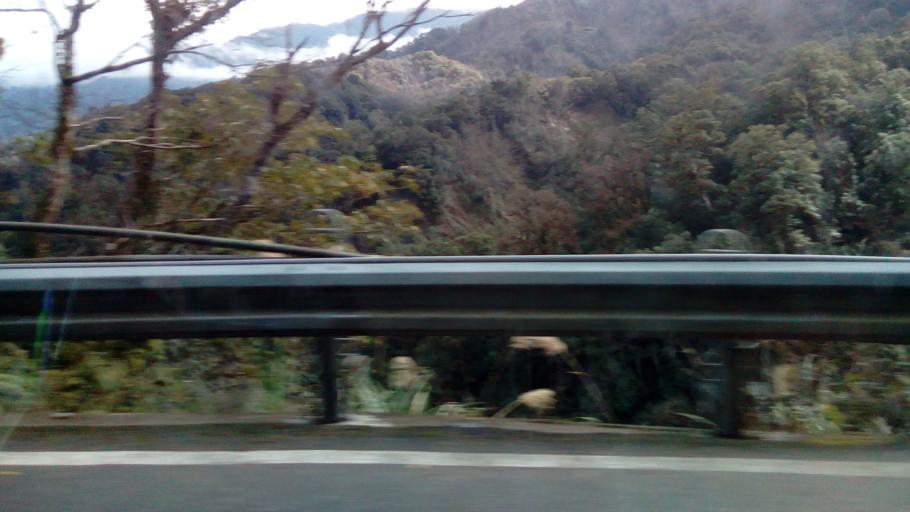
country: TW
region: Taiwan
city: Daxi
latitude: 24.4082
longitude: 121.3588
